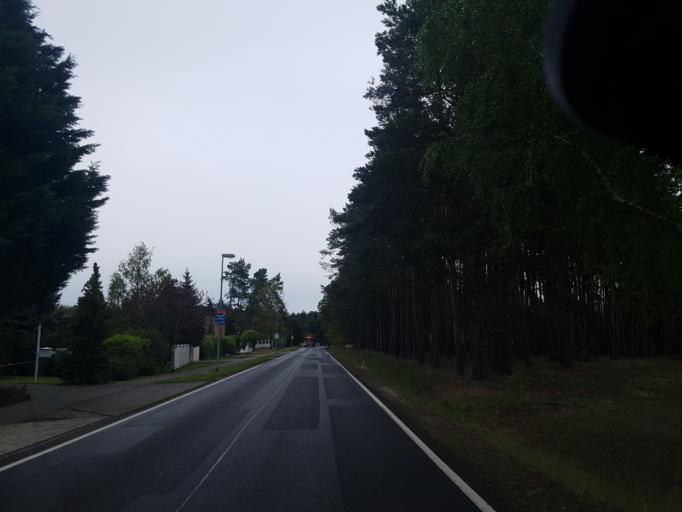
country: DE
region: Brandenburg
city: Spremberg
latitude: 51.6553
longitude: 14.4336
